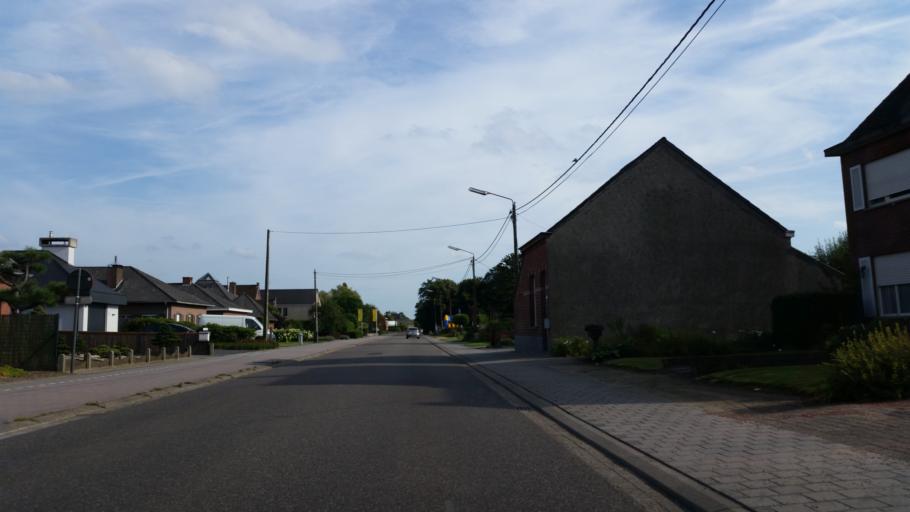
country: BE
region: Flanders
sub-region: Provincie Antwerpen
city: Westerlo
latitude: 51.1163
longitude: 4.9110
